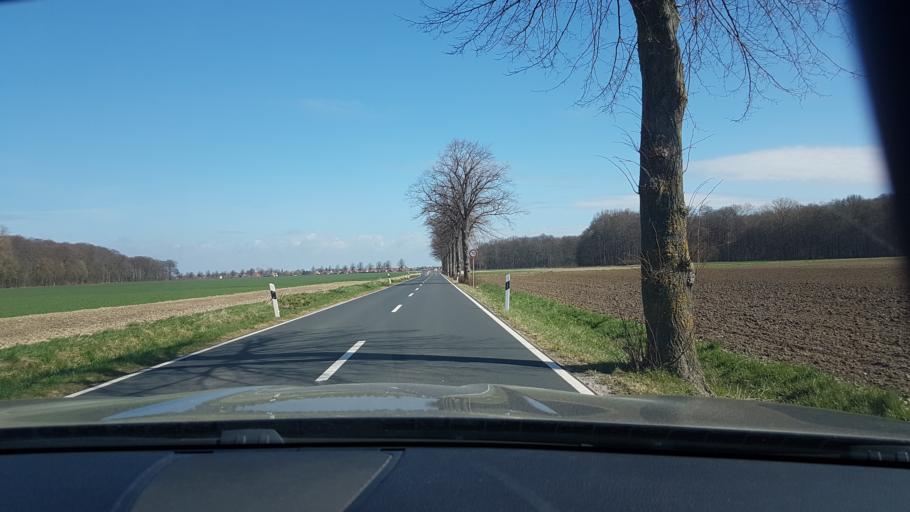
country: DE
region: Lower Saxony
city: Pattensen
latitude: 52.2266
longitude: 9.7183
